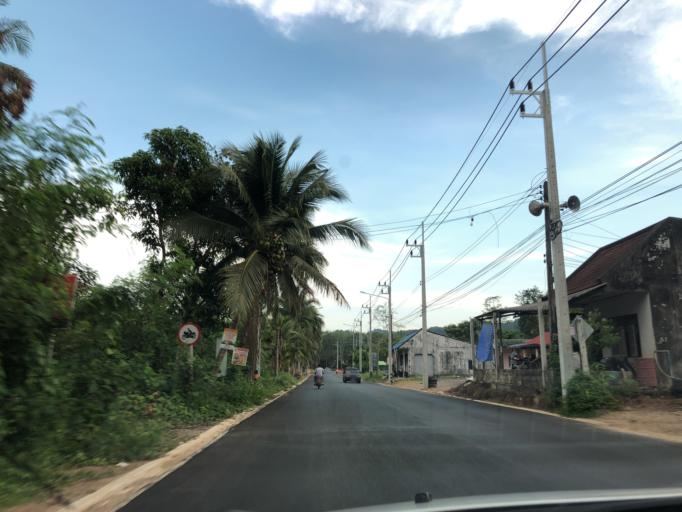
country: TH
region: Phangnga
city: Ban Ao Nang
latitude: 8.0726
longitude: 98.8378
